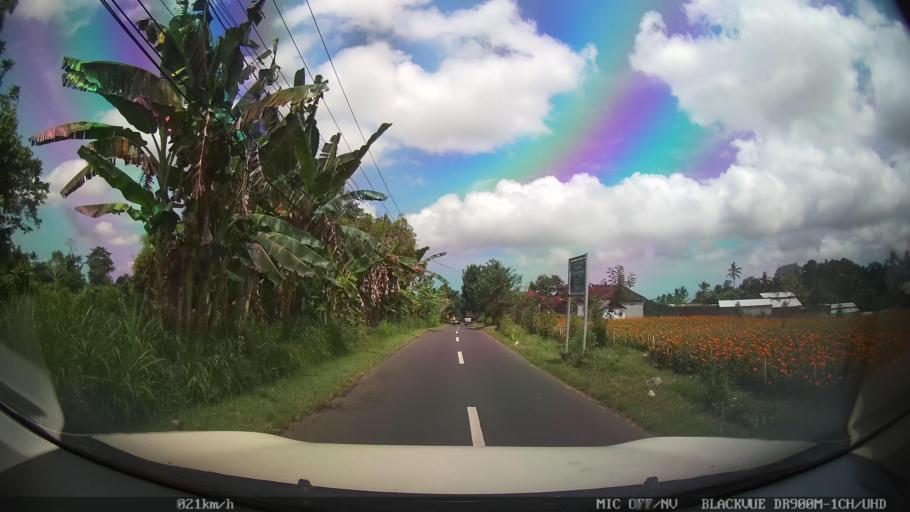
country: ID
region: Bali
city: Banjar Kelodan
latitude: -8.5163
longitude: 115.3798
